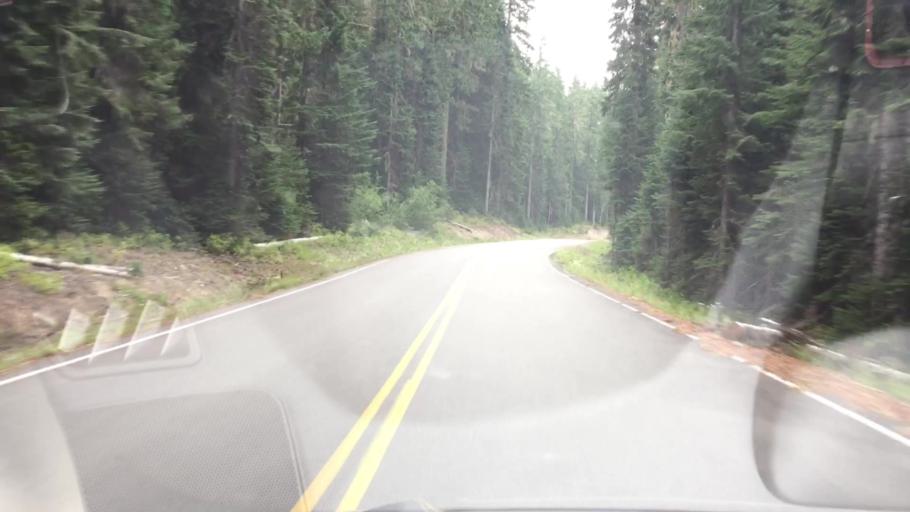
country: US
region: Washington
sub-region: Klickitat County
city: White Salmon
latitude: 46.1666
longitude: -121.6308
